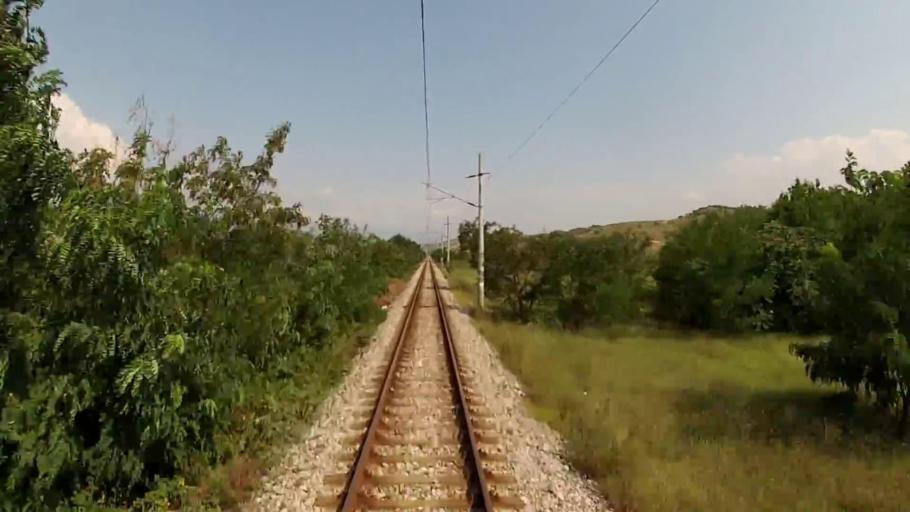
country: BG
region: Blagoevgrad
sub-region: Obshtina Strumyani
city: Strumyani
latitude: 41.6111
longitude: 23.2237
